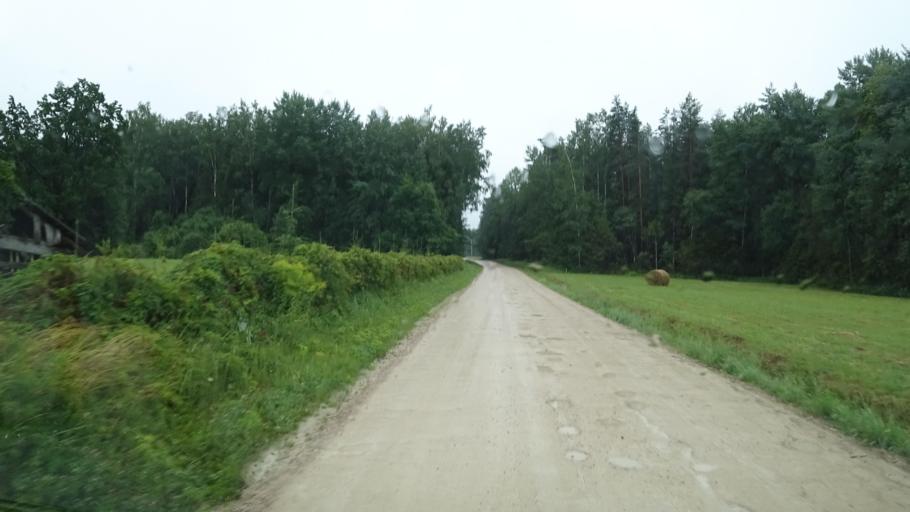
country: LV
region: Lecava
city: Iecava
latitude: 56.6461
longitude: 24.1728
